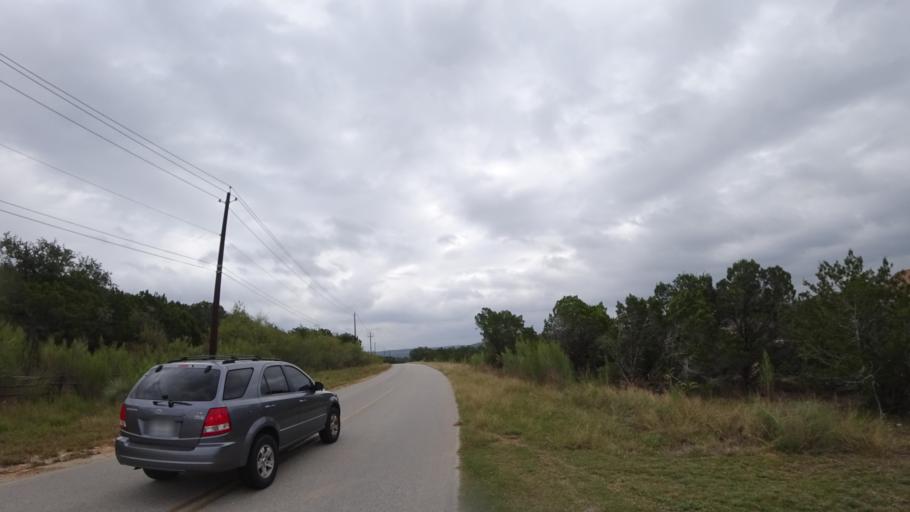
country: US
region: Texas
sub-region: Travis County
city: Bee Cave
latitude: 30.3381
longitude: -97.9196
